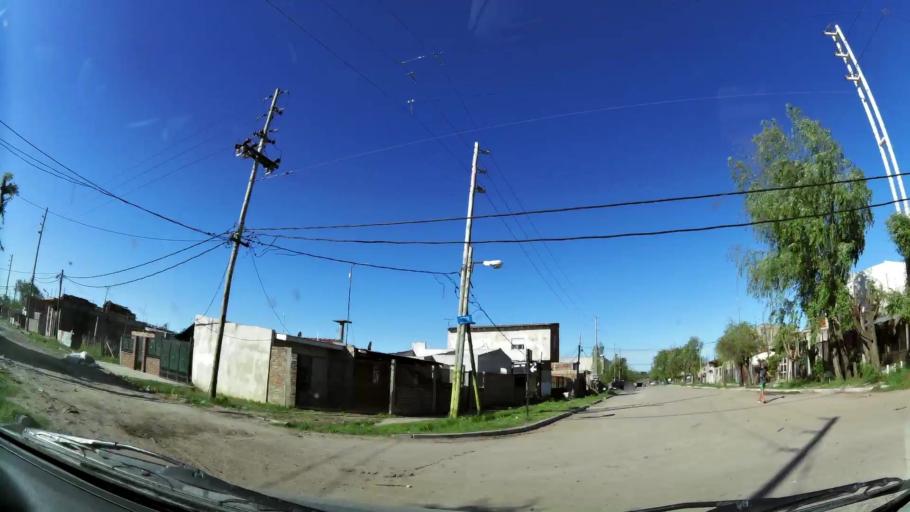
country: AR
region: Buenos Aires
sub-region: Partido de Quilmes
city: Quilmes
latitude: -34.7586
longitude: -58.3194
